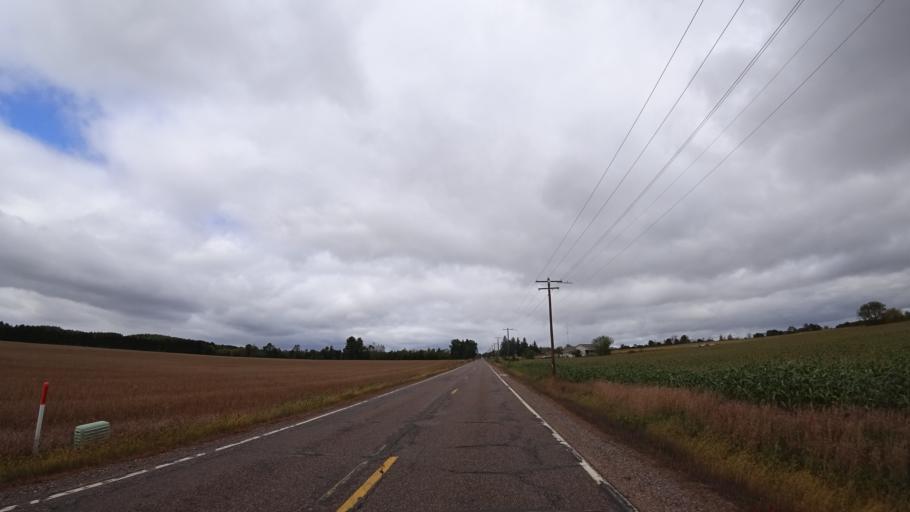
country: US
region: Wisconsin
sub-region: Chippewa County
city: Lake Wissota
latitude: 44.9665
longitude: -91.2678
